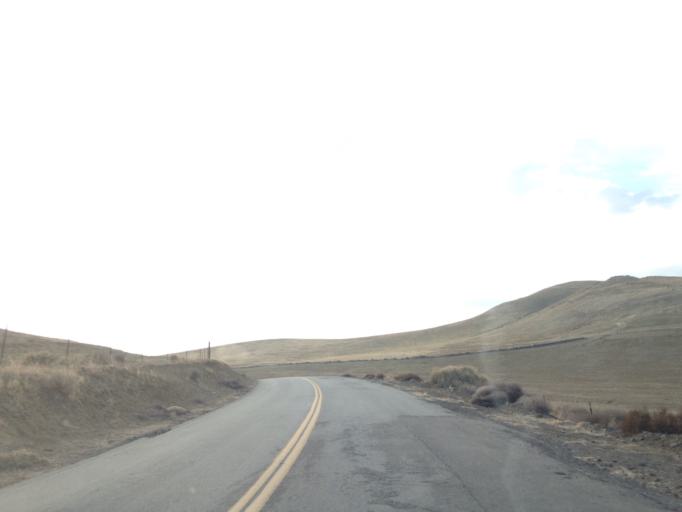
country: US
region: California
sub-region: Kings County
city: Kettleman City
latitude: 35.7277
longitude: -120.0254
